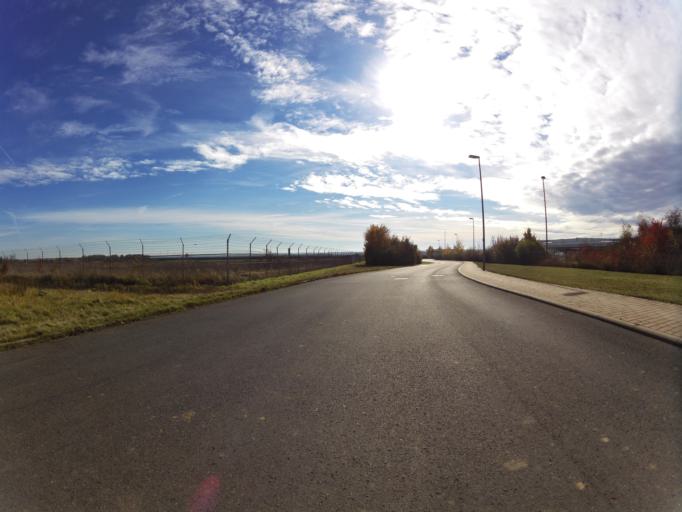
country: DE
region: Bavaria
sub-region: Regierungsbezirk Unterfranken
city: Giebelstadt
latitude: 49.6543
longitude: 9.9600
